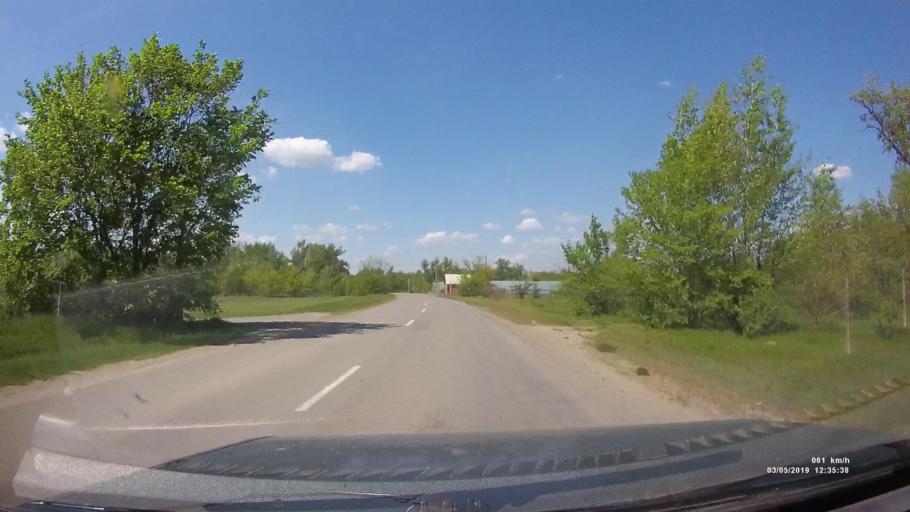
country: RU
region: Rostov
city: Semikarakorsk
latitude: 47.5281
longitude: 40.7593
